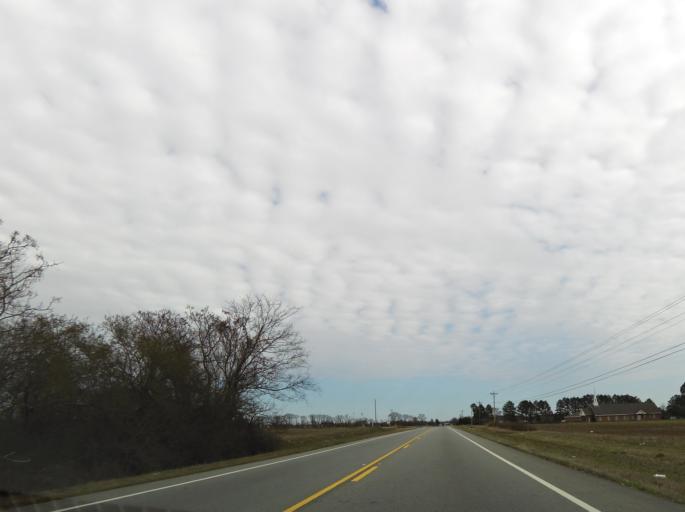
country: US
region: Georgia
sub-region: Peach County
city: Byron
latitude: 32.6065
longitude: -83.7760
